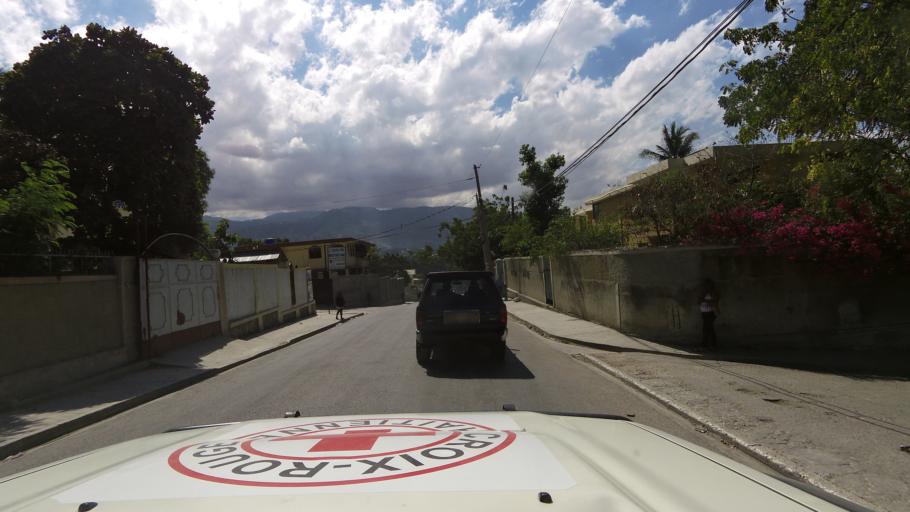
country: HT
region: Ouest
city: Delmas 73
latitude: 18.5644
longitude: -72.2995
